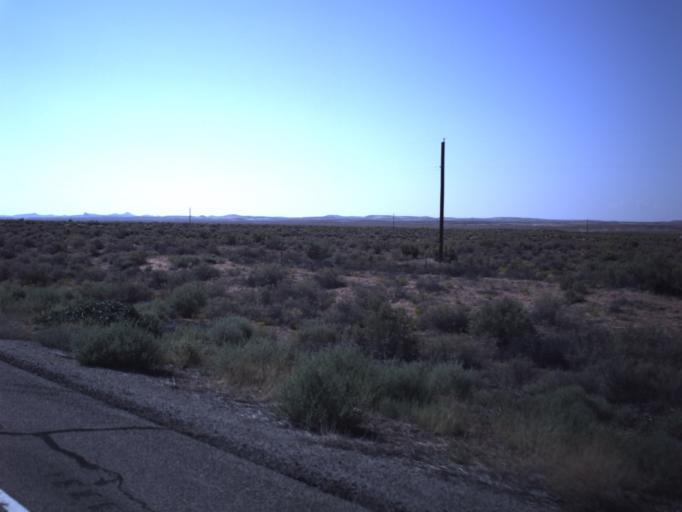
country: US
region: Utah
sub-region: San Juan County
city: Blanding
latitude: 37.1907
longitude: -109.5960
